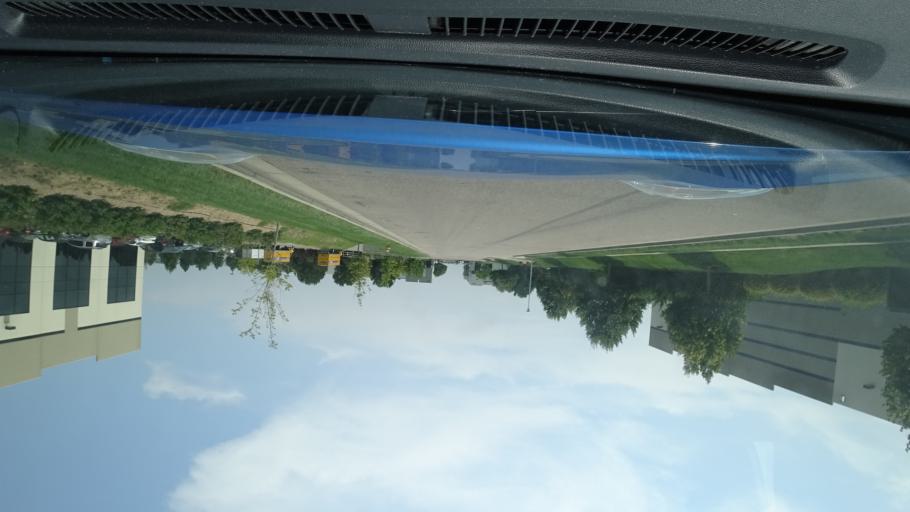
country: US
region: Colorado
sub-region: Adams County
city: Aurora
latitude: 39.7652
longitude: -104.7601
